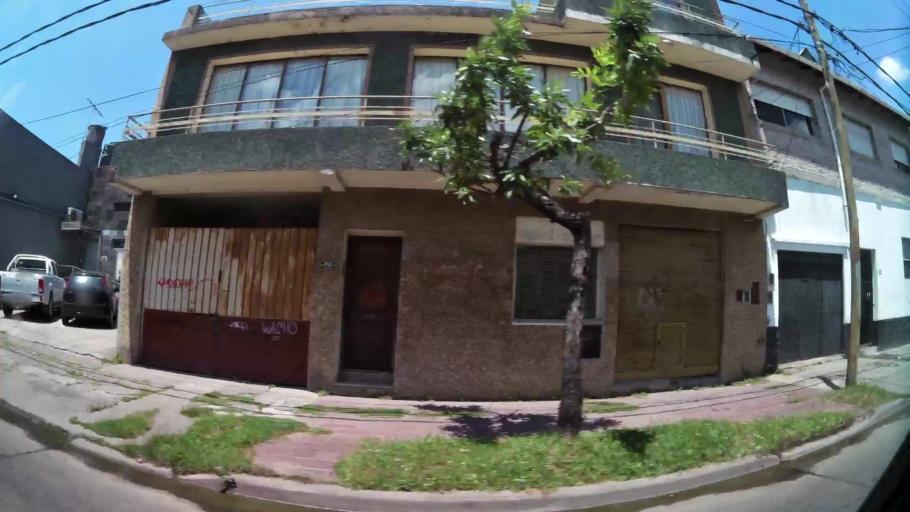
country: AR
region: Buenos Aires
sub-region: Partido de Tigre
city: Tigre
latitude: -34.4204
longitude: -58.5909
